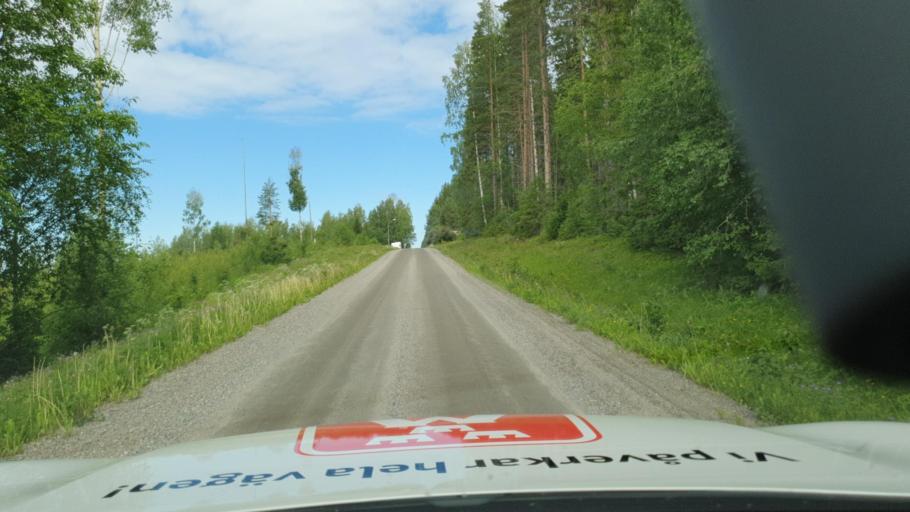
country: SE
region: Vaesterbotten
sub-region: Skelleftea Kommun
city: Forsbacka
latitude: 64.6487
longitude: 20.5388
